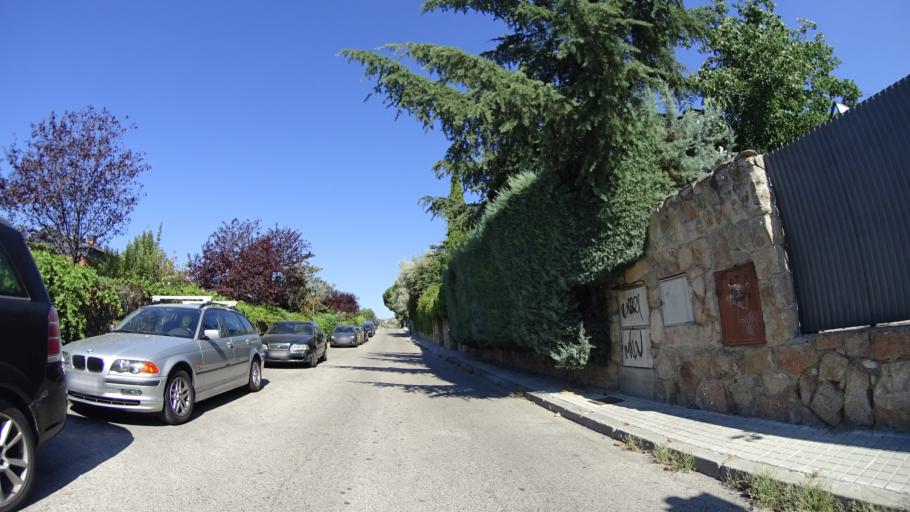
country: ES
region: Madrid
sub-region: Provincia de Madrid
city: Torrelodones
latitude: 40.5784
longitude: -3.9232
